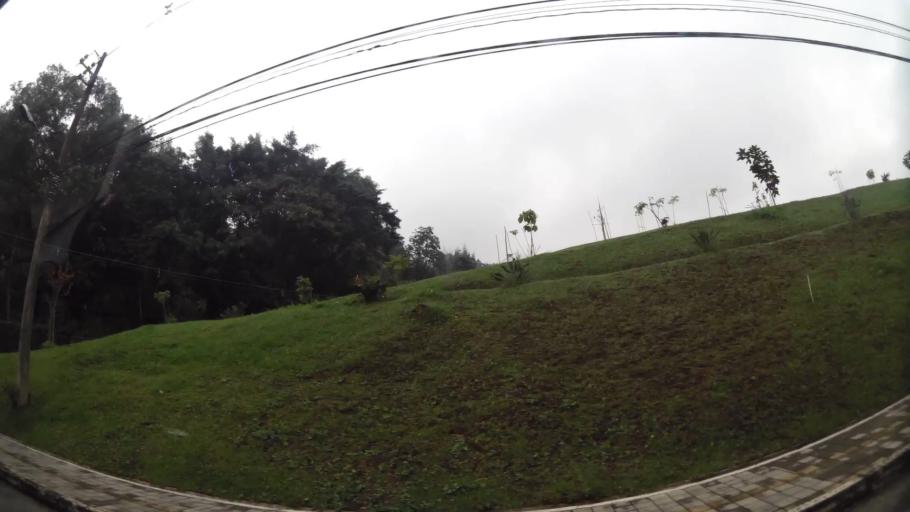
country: CO
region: Antioquia
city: Envigado
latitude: 6.1908
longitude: -75.5544
